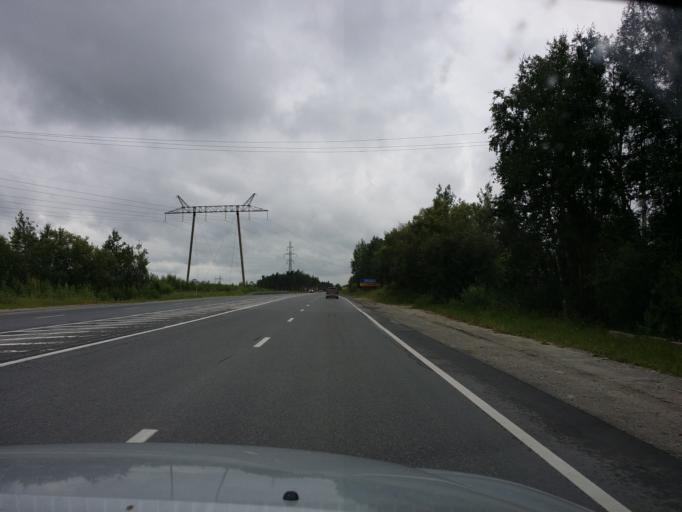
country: RU
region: Khanty-Mansiyskiy Avtonomnyy Okrug
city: Megion
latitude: 61.0478
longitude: 76.3422
